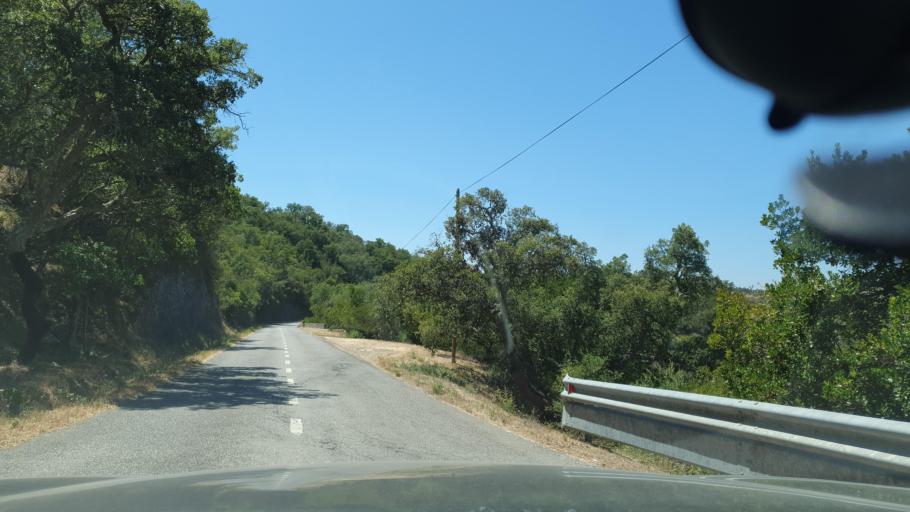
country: PT
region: Beja
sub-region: Odemira
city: Odemira
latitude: 37.6028
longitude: -8.5713
